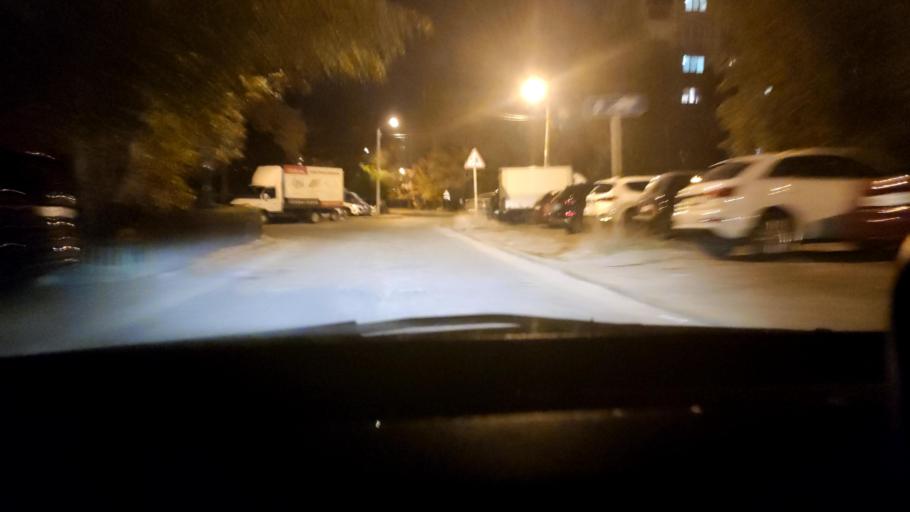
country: RU
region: Voronezj
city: Podgornoye
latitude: 51.7187
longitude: 39.1711
